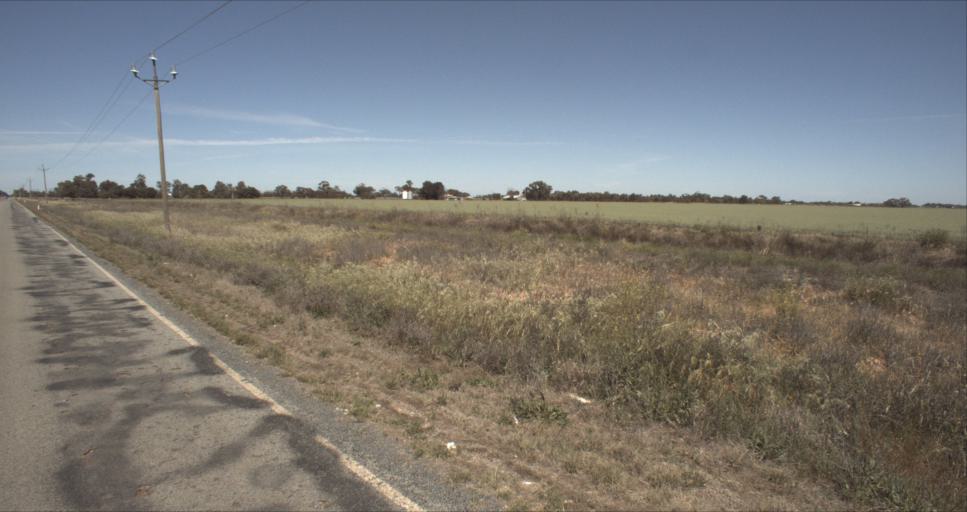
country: AU
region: New South Wales
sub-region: Leeton
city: Leeton
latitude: -34.5092
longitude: 146.2854
